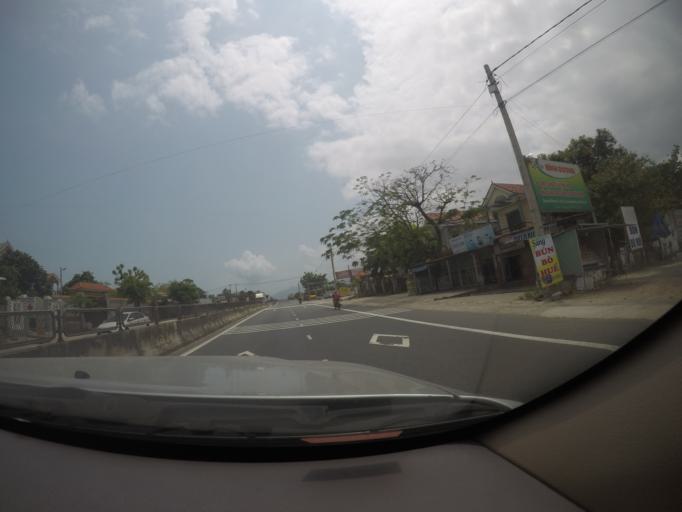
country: VN
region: Thua Thien-Hue
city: Phu Loc
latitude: 16.2578
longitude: 108.0625
